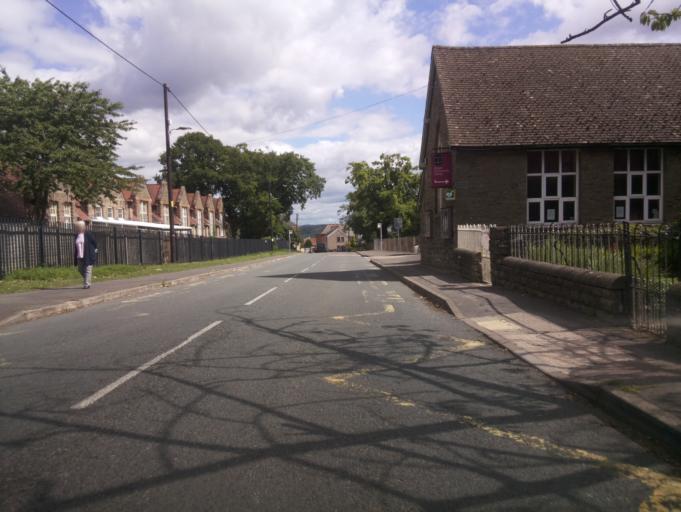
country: GB
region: England
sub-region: Gloucestershire
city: Bream
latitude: 51.7510
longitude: -2.5740
